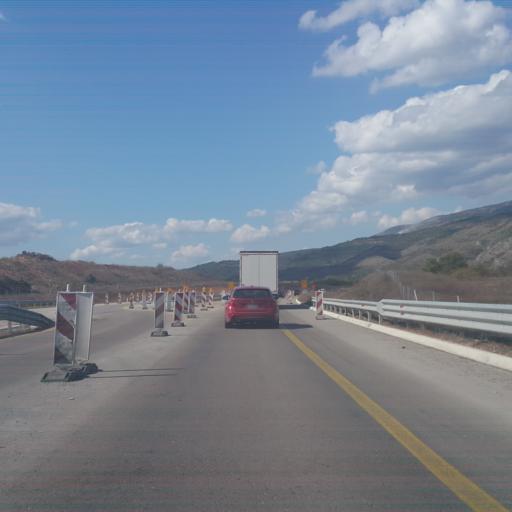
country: RS
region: Central Serbia
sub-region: Pirotski Okrug
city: Bela Palanka
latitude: 43.2260
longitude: 22.3861
